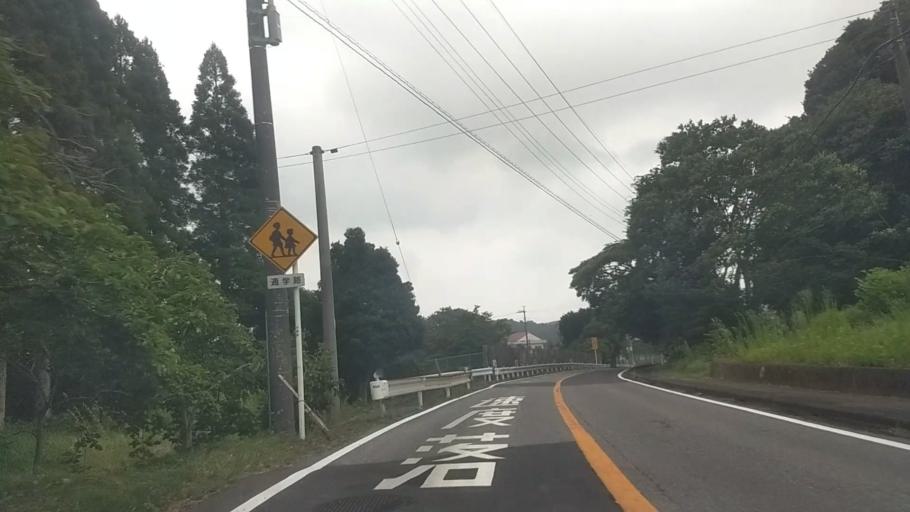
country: JP
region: Chiba
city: Katsuura
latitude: 35.2502
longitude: 140.2139
